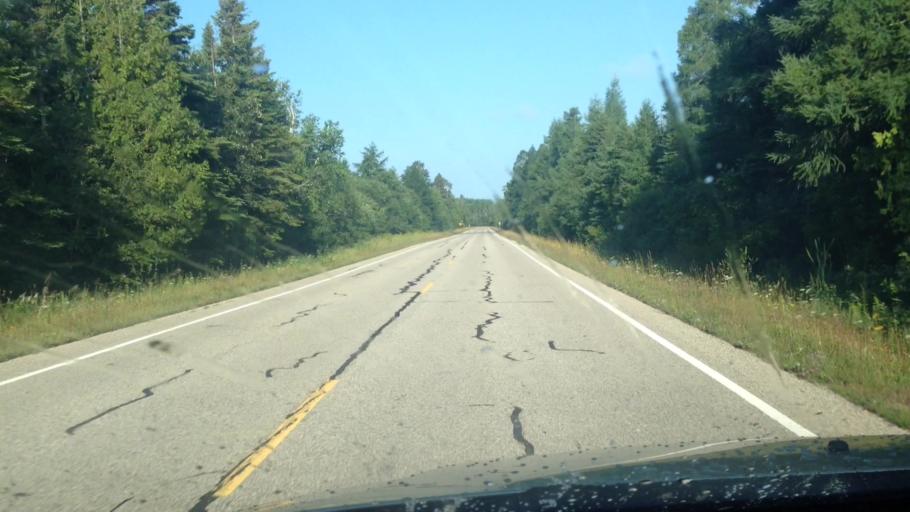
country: US
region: Michigan
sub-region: Mackinac County
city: Saint Ignace
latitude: 45.8930
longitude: -84.7767
